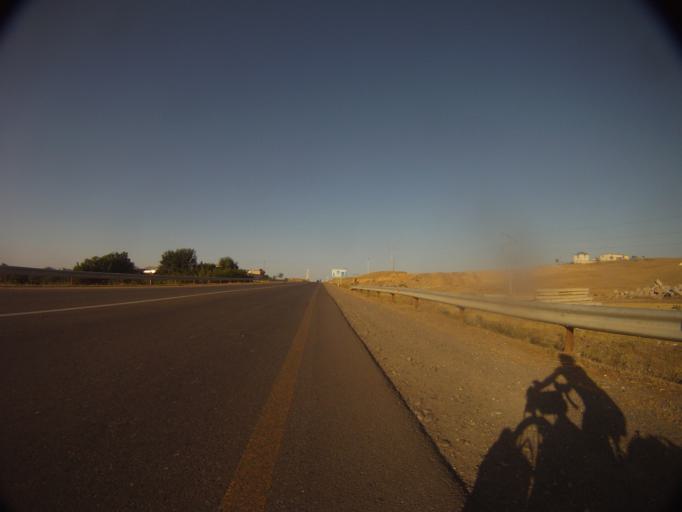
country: AZ
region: Qazax
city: Qazax
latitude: 41.0835
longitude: 45.3779
